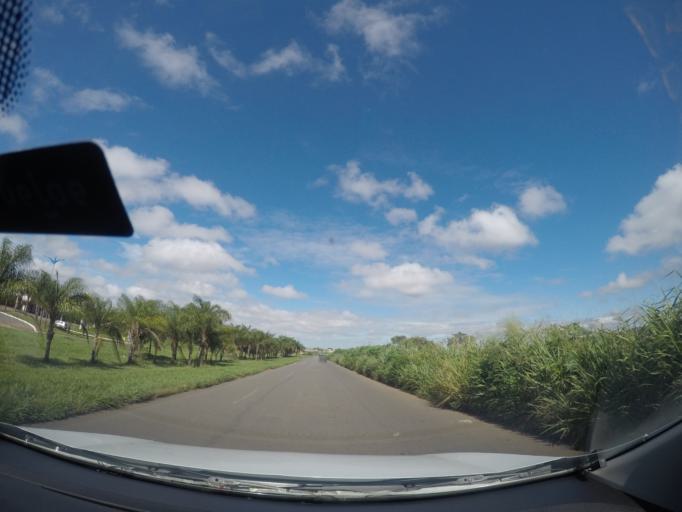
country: BR
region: Goias
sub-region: Senador Canedo
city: Senador Canedo
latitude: -16.6491
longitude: -49.1568
